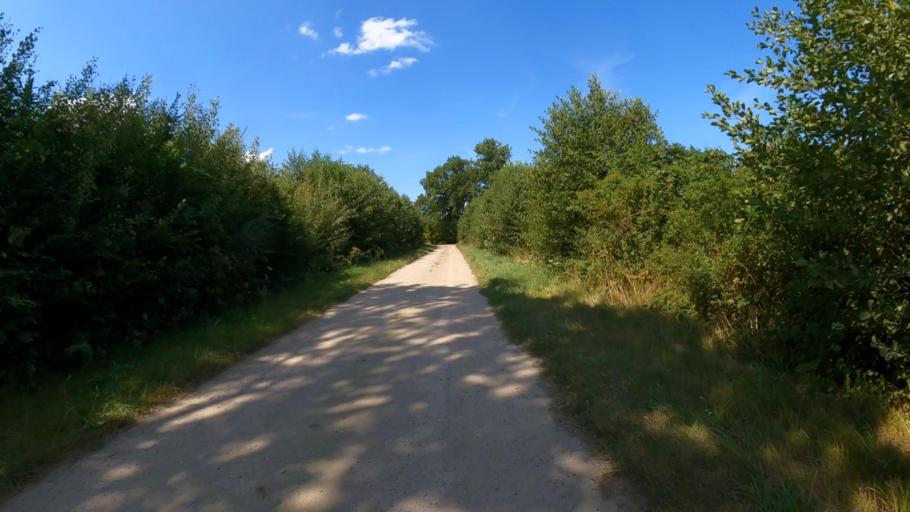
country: DE
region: Schleswig-Holstein
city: Borstel-Hohenraden
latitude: 53.7094
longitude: 9.8297
